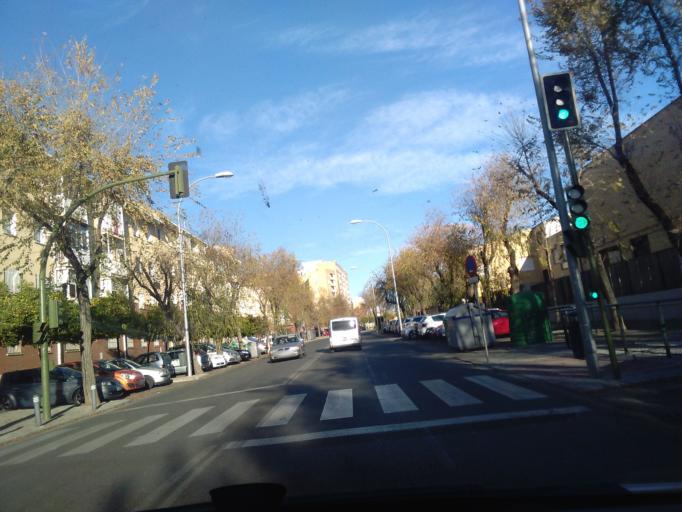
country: ES
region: Andalusia
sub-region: Provincia de Sevilla
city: Sevilla
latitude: 37.3795
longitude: -5.9556
